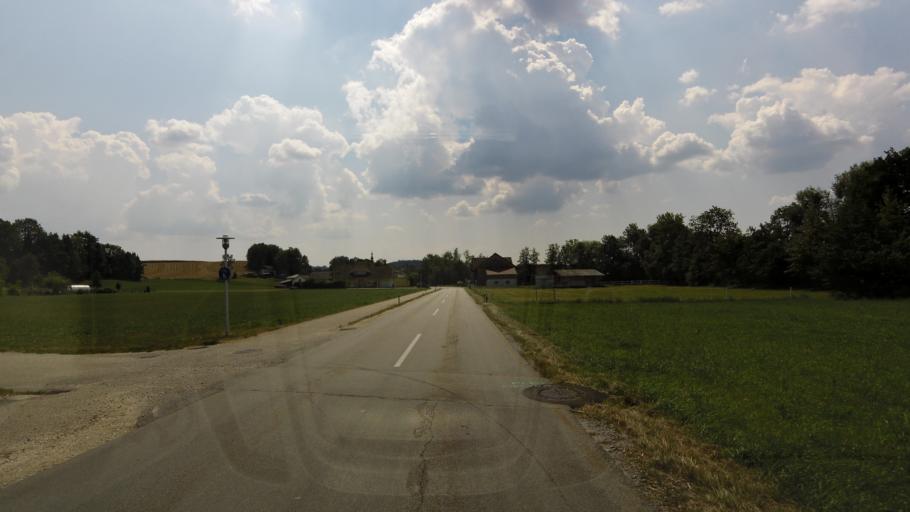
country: AT
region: Upper Austria
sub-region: Politischer Bezirk Ried im Innkreis
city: Waldzell
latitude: 48.1419
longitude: 13.4242
